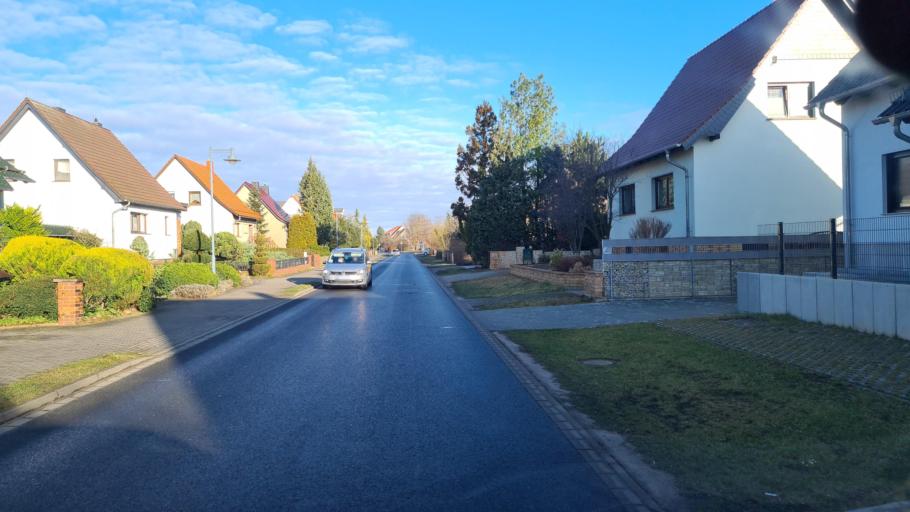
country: DE
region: Brandenburg
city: Herzberg
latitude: 51.6925
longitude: 13.2248
